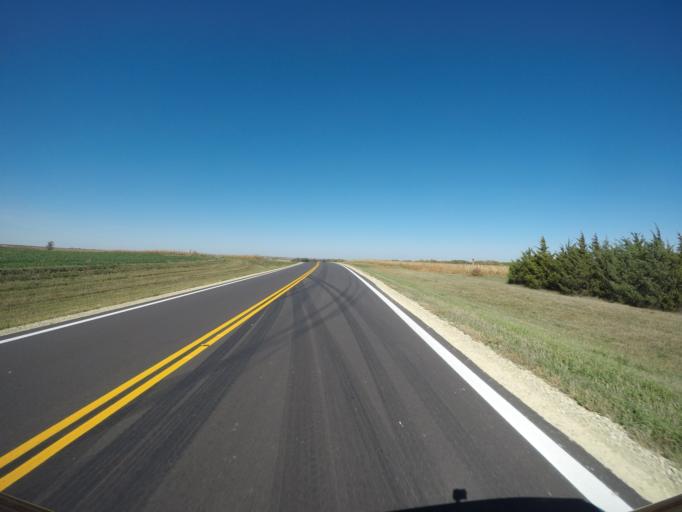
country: US
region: Kansas
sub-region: Mitchell County
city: Beloit
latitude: 39.5597
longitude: -98.3400
